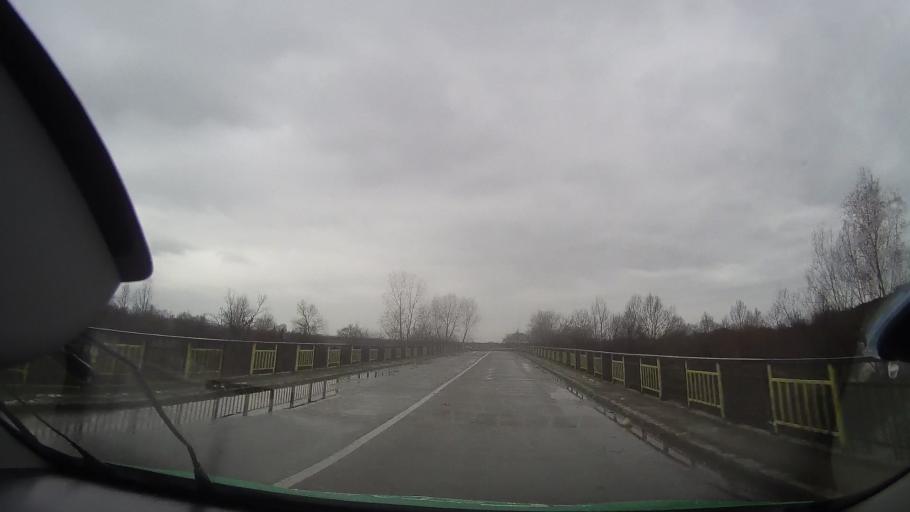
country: RO
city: Capalna
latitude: 46.7336
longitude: 22.0983
